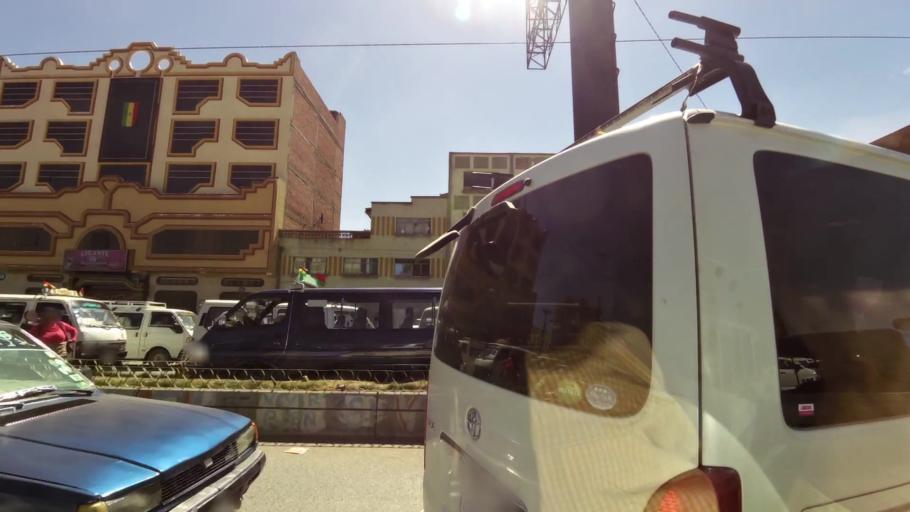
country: BO
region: La Paz
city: La Paz
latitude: -16.4968
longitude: -68.1865
